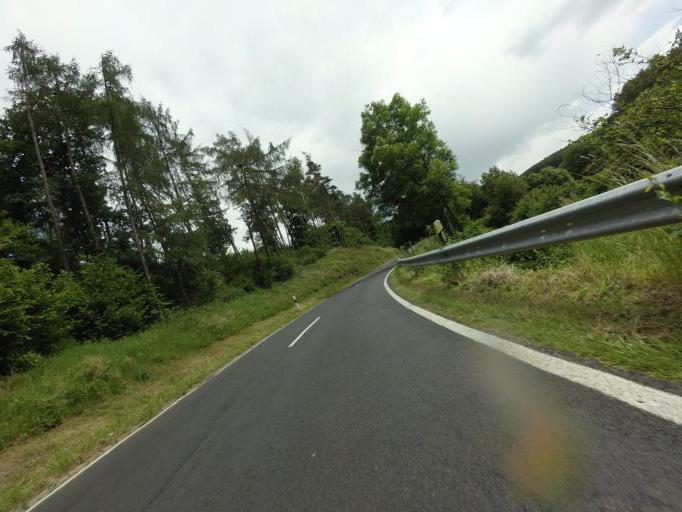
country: DE
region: Rheinland-Pfalz
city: Landkern
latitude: 50.2130
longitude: 7.1525
